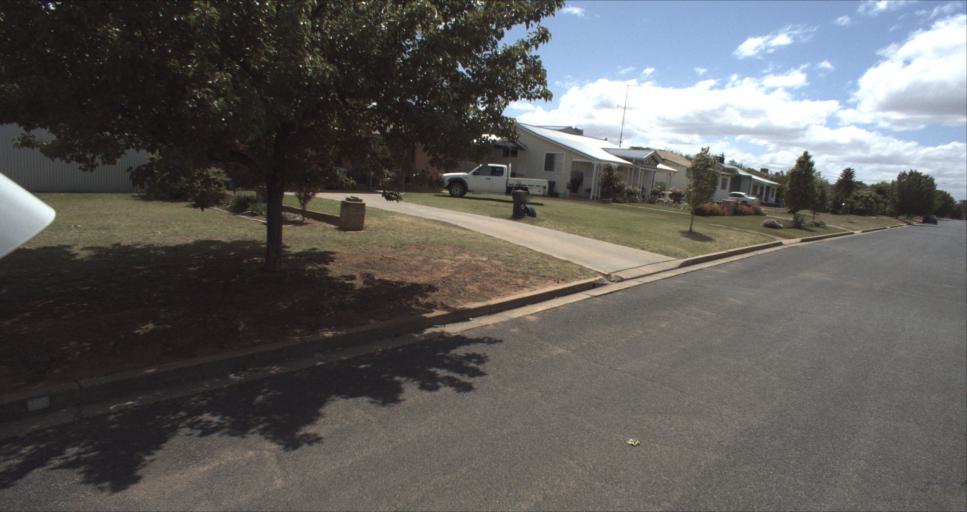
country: AU
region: New South Wales
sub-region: Leeton
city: Leeton
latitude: -34.5616
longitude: 146.3986
